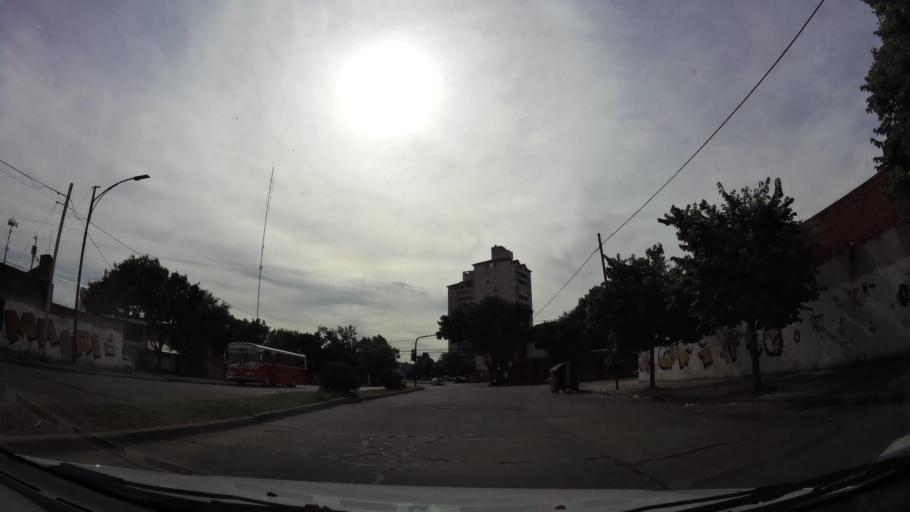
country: AR
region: Buenos Aires F.D.
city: Villa Lugano
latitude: -34.6526
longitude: -58.4865
